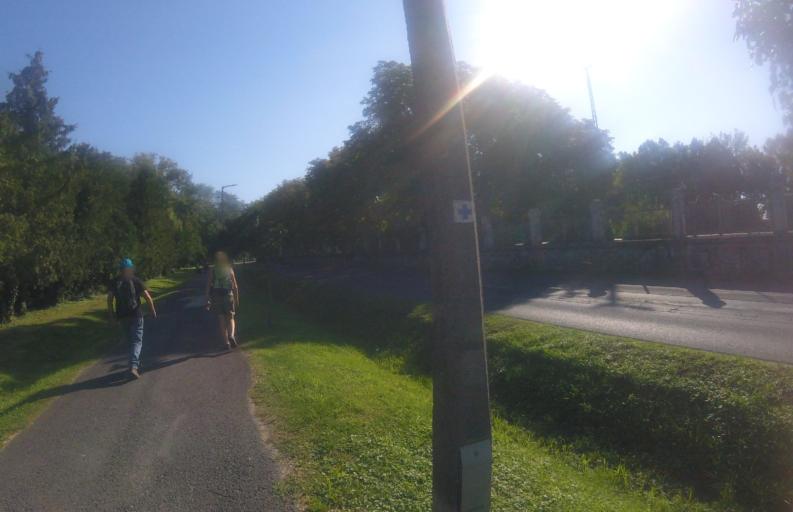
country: HU
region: Zala
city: Keszthely
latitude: 46.7590
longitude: 17.2481
